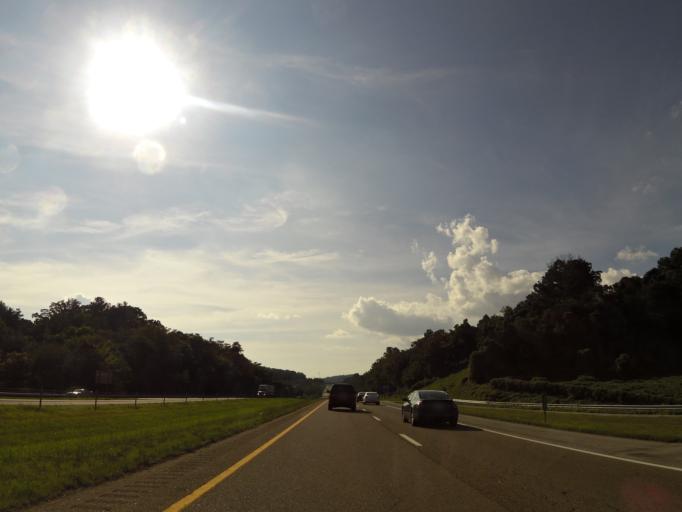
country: US
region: Tennessee
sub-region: Blount County
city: Alcoa
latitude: 35.8375
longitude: -83.9734
